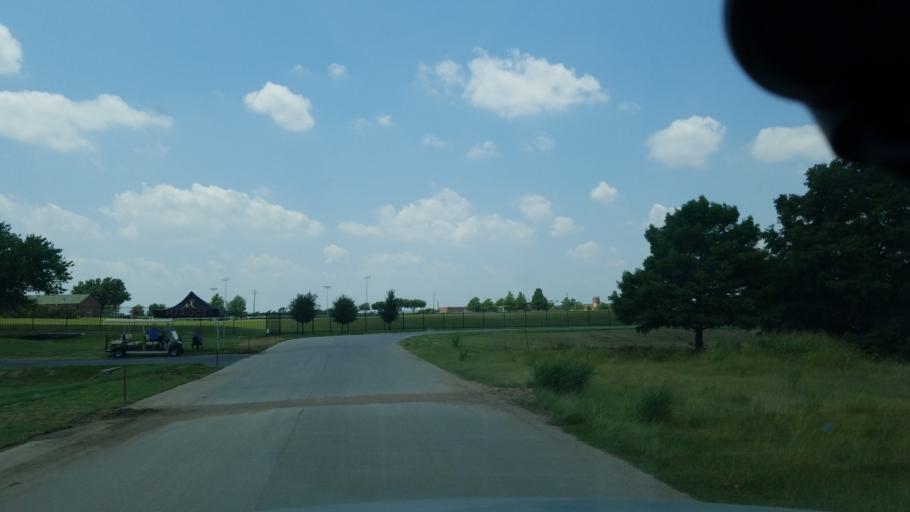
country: US
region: Texas
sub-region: Dallas County
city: Carrollton
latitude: 32.9636
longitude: -96.8741
